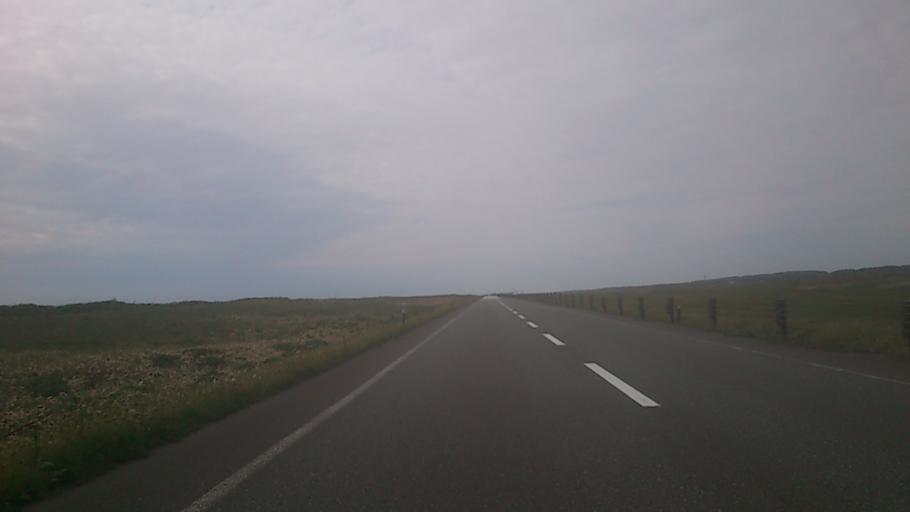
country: JP
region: Hokkaido
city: Wakkanai
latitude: 45.0640
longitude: 141.6449
